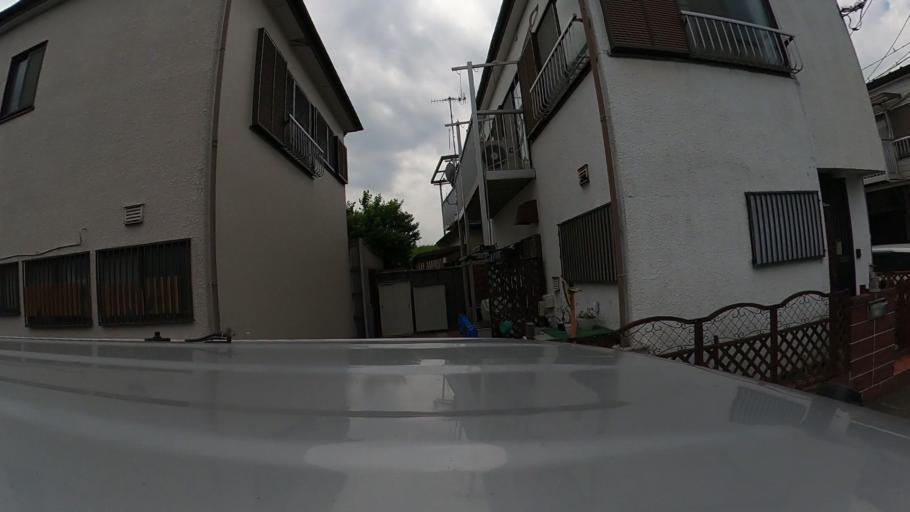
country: JP
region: Kanagawa
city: Chigasaki
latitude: 35.3591
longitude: 139.3726
